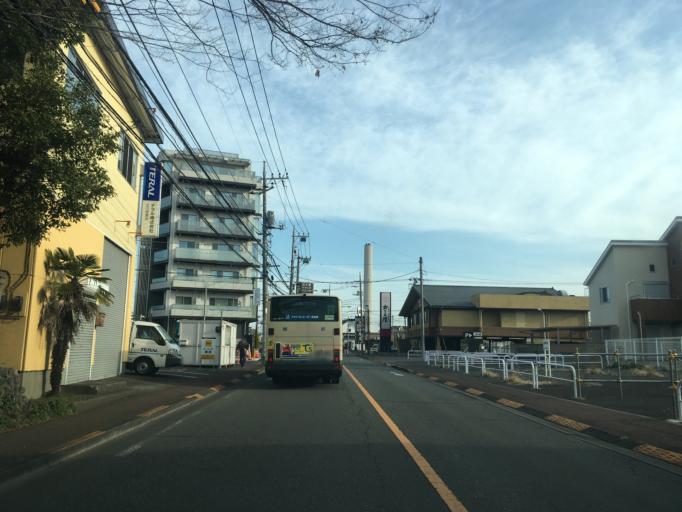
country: JP
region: Tokyo
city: Kokubunji
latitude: 35.7208
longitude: 139.4325
